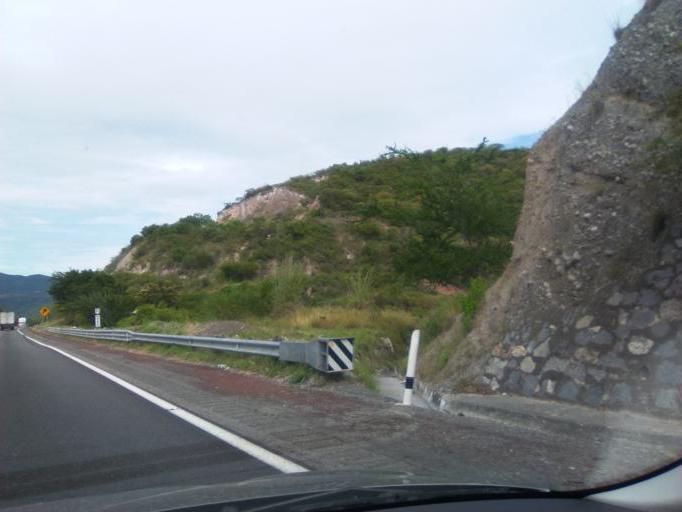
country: MX
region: Guerrero
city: Zumpango del Rio
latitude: 17.6202
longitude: -99.5179
